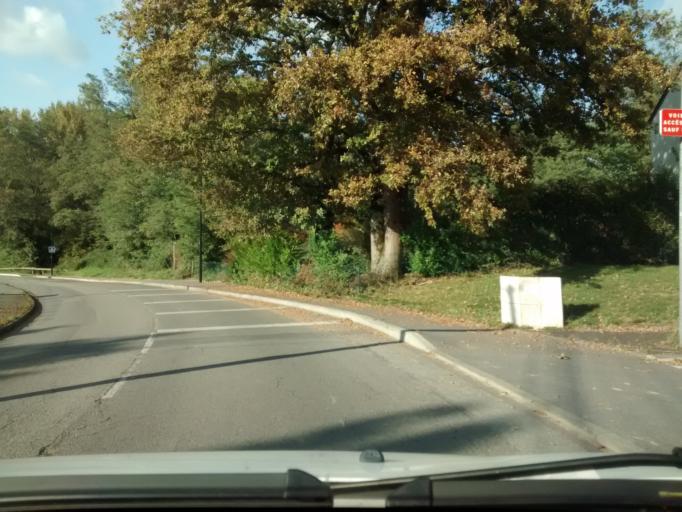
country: FR
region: Pays de la Loire
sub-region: Departement de la Loire-Atlantique
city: Sautron
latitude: 47.2676
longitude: -1.6701
